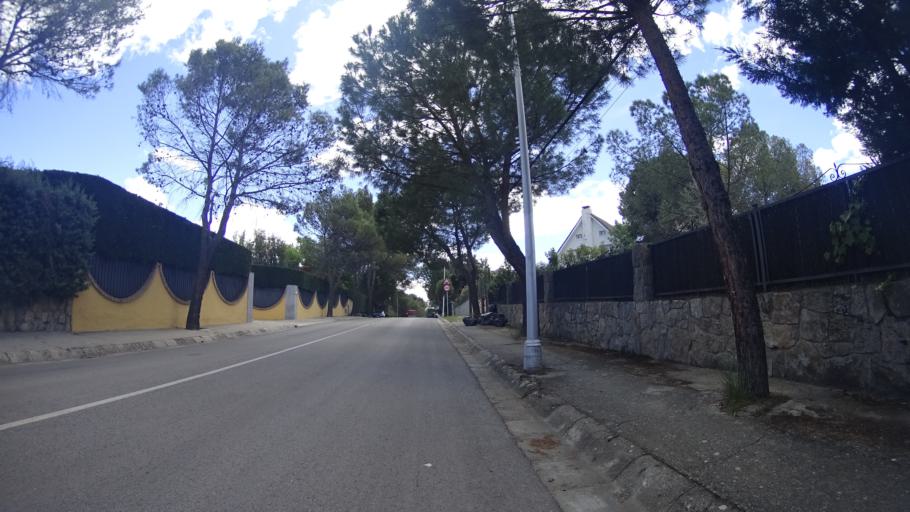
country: ES
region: Madrid
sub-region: Provincia de Madrid
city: Villaviciosa de Odon
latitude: 40.3763
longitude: -3.9343
